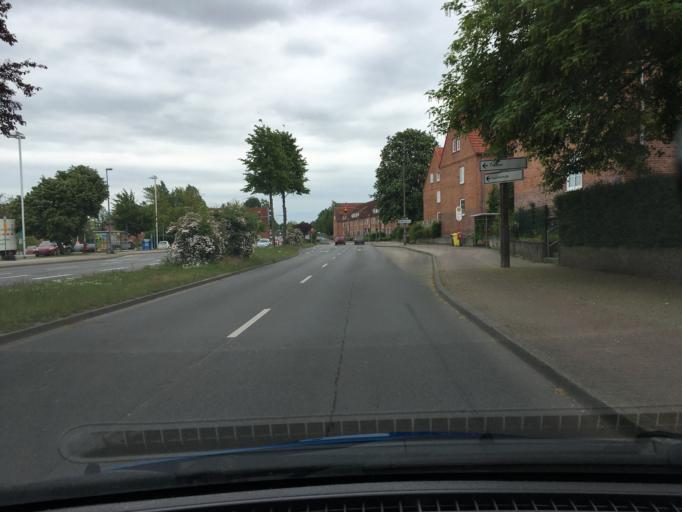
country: DE
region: Mecklenburg-Vorpommern
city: Wismar
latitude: 53.8893
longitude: 11.4428
